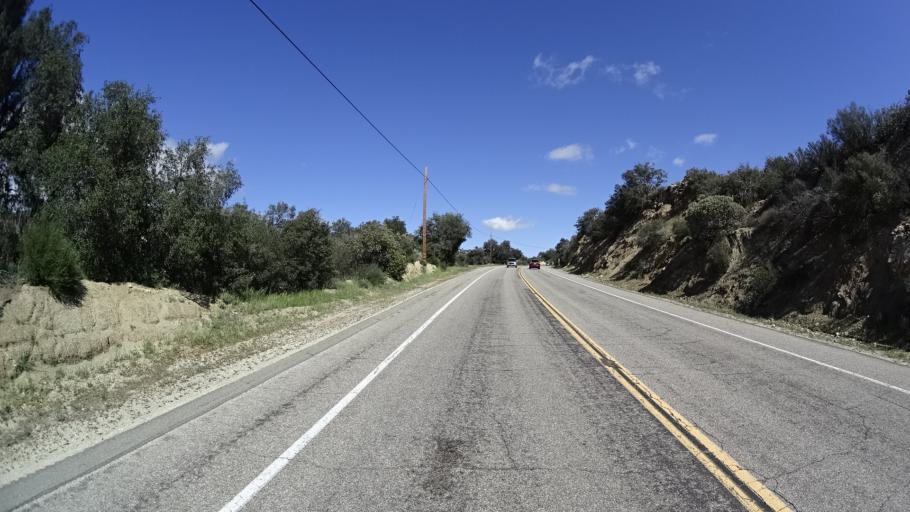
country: US
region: California
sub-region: San Diego County
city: Julian
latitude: 33.2134
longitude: -116.5580
